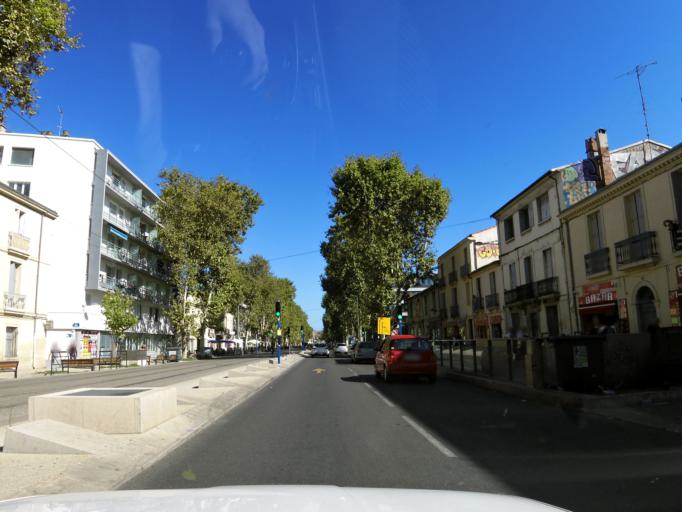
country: FR
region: Languedoc-Roussillon
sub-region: Departement de l'Herault
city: Montpellier
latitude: 43.6081
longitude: 3.8689
